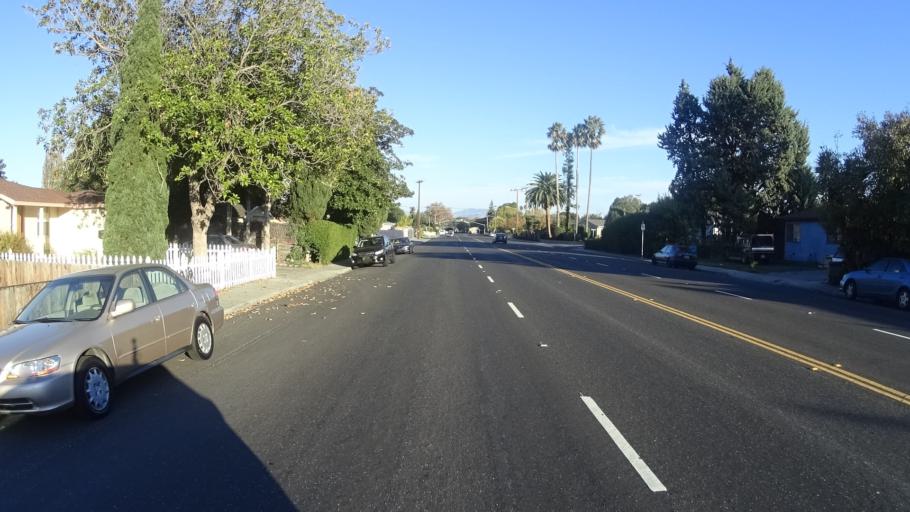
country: US
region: California
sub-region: Santa Clara County
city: Santa Clara
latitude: 37.3633
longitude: -121.9787
